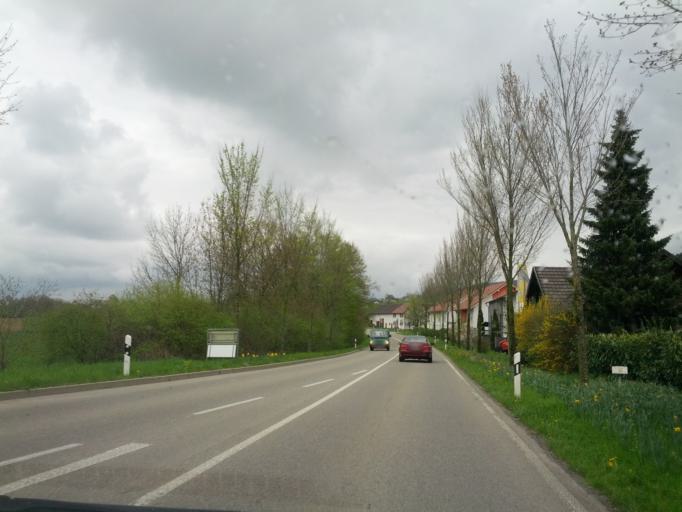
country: DE
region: Baden-Wuerttemberg
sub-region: Freiburg Region
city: Solden
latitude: 47.9339
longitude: 7.8106
